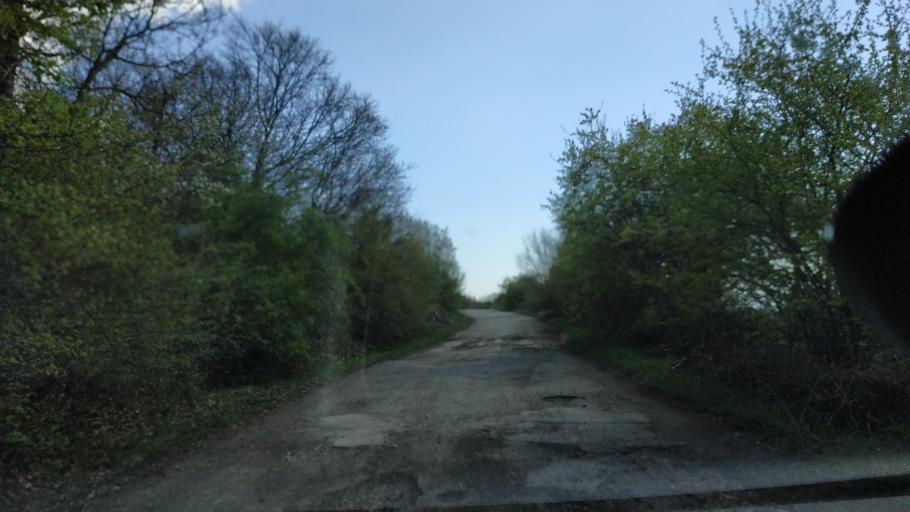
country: RS
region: Central Serbia
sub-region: Zajecarski Okrug
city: Soko Banja
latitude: 43.5617
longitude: 21.8945
